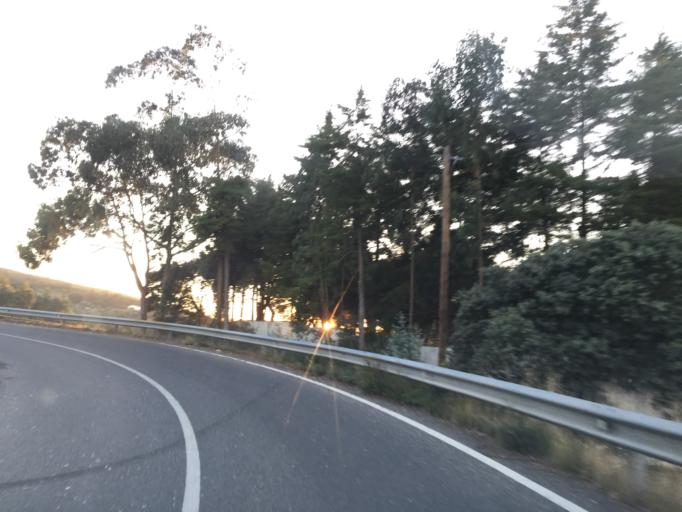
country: PT
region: Santarem
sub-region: Ourem
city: Fatima
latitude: 39.6299
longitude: -8.6234
